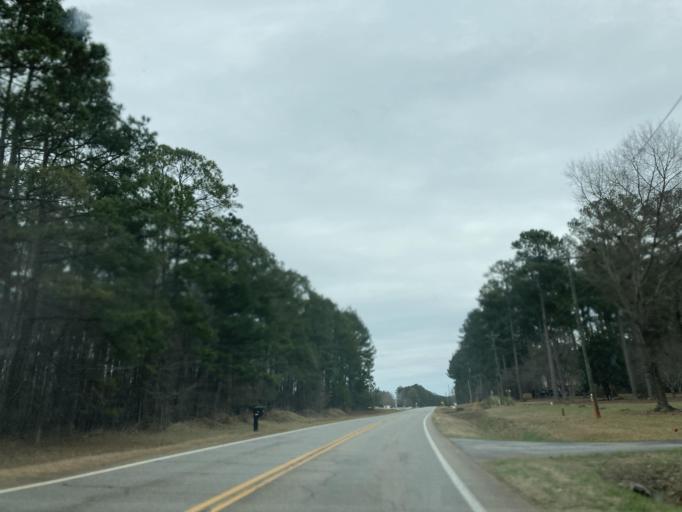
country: US
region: Georgia
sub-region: Jones County
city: Gray
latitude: 32.9935
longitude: -83.5895
